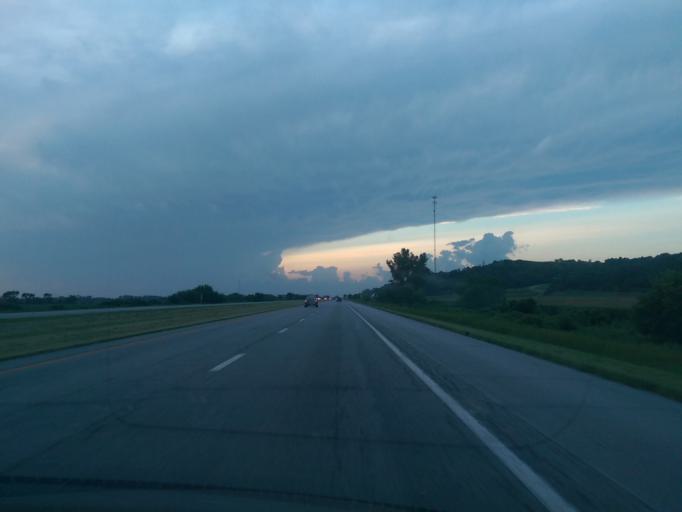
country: US
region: Iowa
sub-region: Fremont County
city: Hamburg
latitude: 40.5384
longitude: -95.6189
